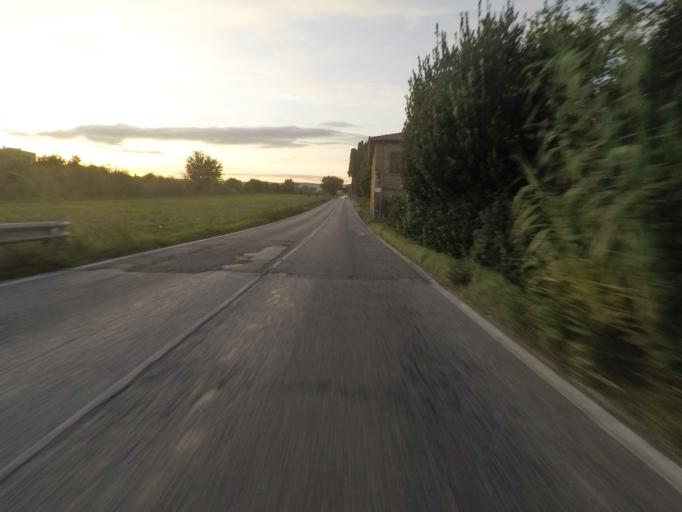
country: IT
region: Tuscany
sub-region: Provincia di Siena
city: Torrita di Siena
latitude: 43.1869
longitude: 11.7628
